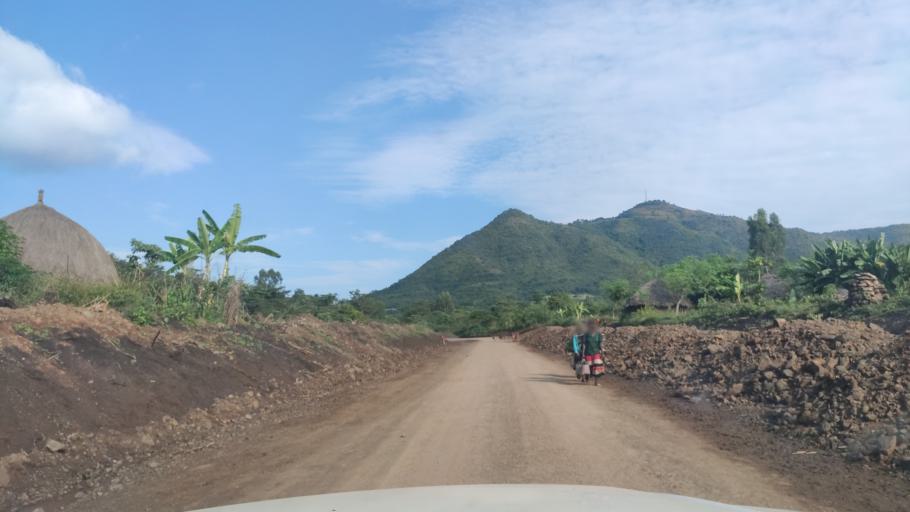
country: ET
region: Southern Nations, Nationalities, and People's Region
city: Arba Minch'
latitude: 6.4266
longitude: 37.3296
